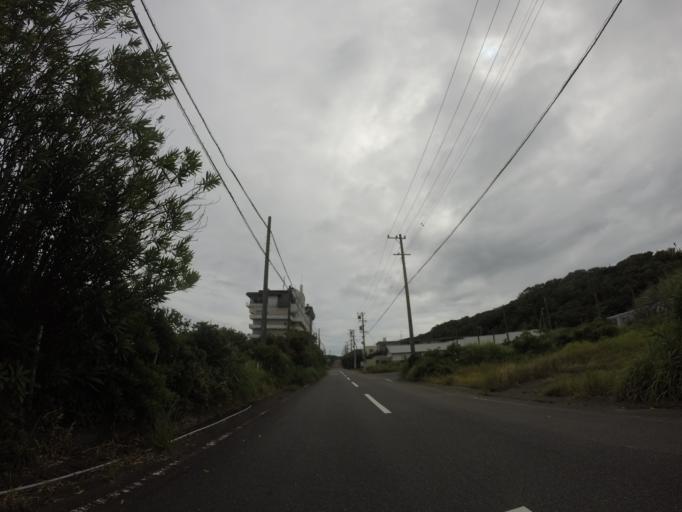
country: JP
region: Shizuoka
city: Oyama
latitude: 34.5993
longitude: 138.2311
